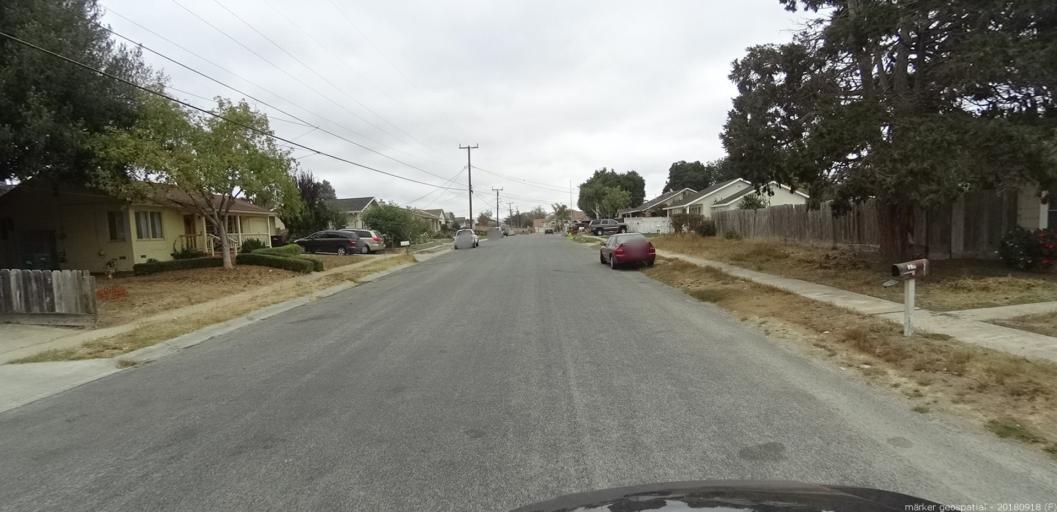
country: US
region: California
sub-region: Monterey County
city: Prunedale
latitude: 36.7358
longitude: -121.6383
